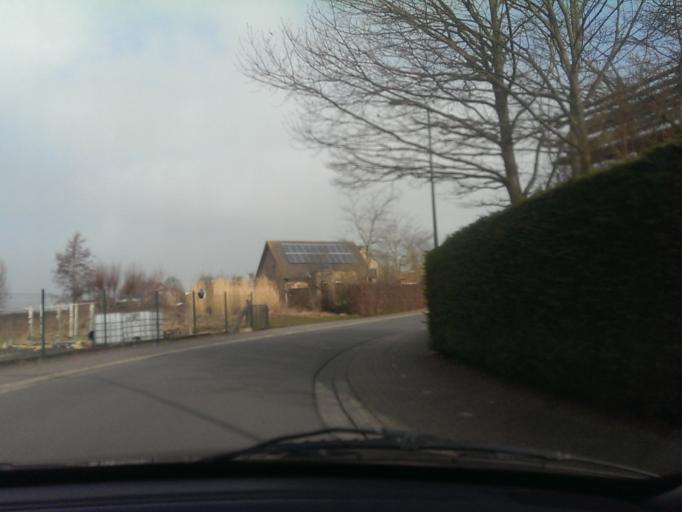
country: BE
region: Flanders
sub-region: Provincie West-Vlaanderen
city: Roeselare
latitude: 50.9347
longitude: 3.0937
